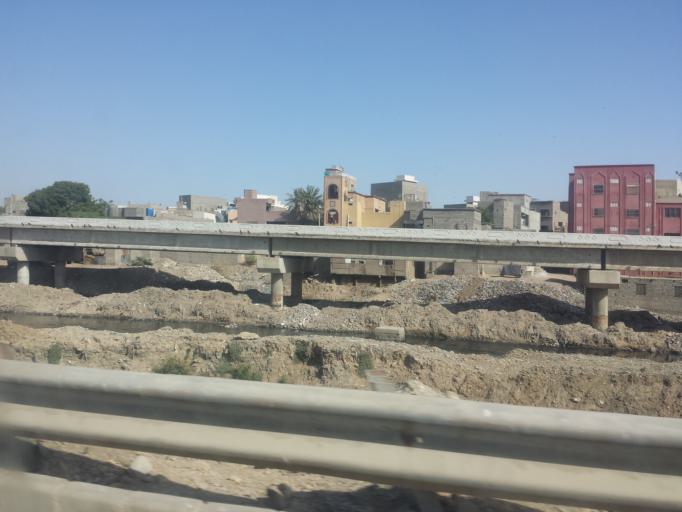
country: PK
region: Sindh
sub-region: Karachi District
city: Karachi
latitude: 24.8946
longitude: 67.0480
